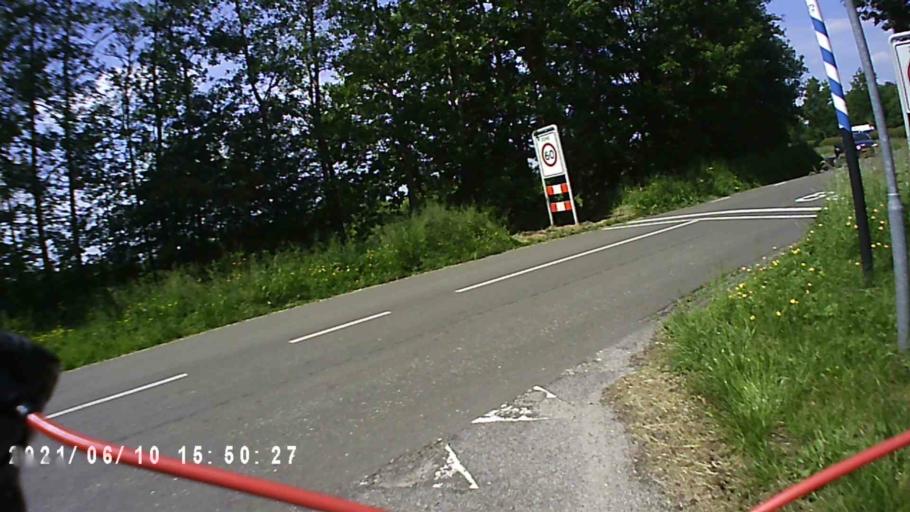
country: NL
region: Friesland
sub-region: Gemeente Achtkarspelen
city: Harkema
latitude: 53.1695
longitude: 6.1185
